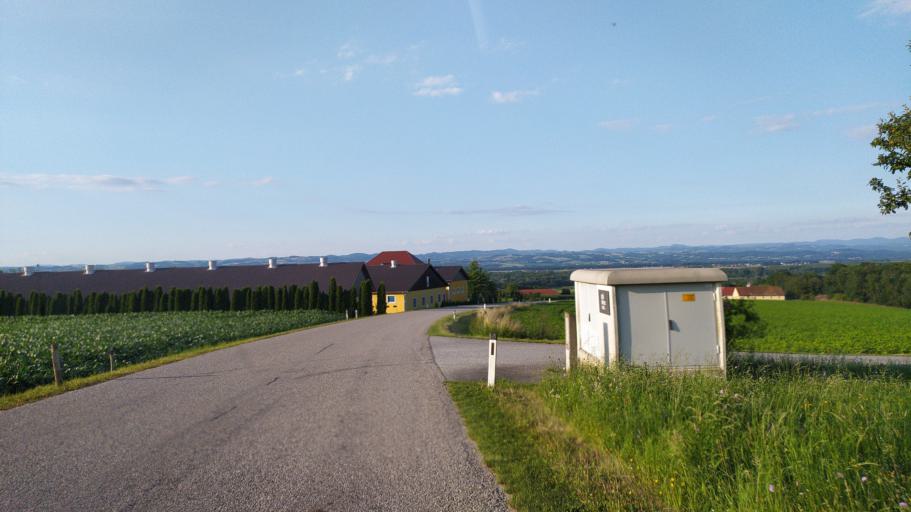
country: AT
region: Lower Austria
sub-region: Politischer Bezirk Amstetten
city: Strengberg
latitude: 48.1641
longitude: 14.6181
